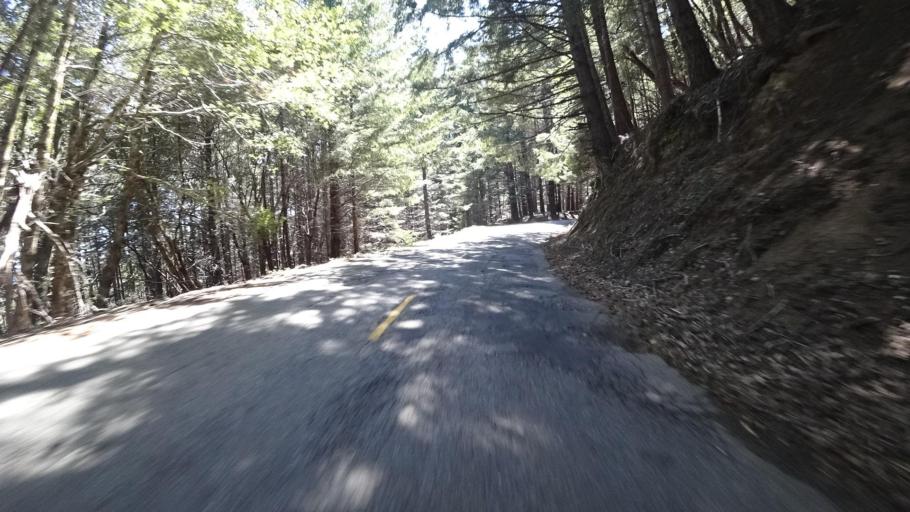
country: US
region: California
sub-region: Humboldt County
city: Rio Dell
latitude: 40.3004
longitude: -124.0557
